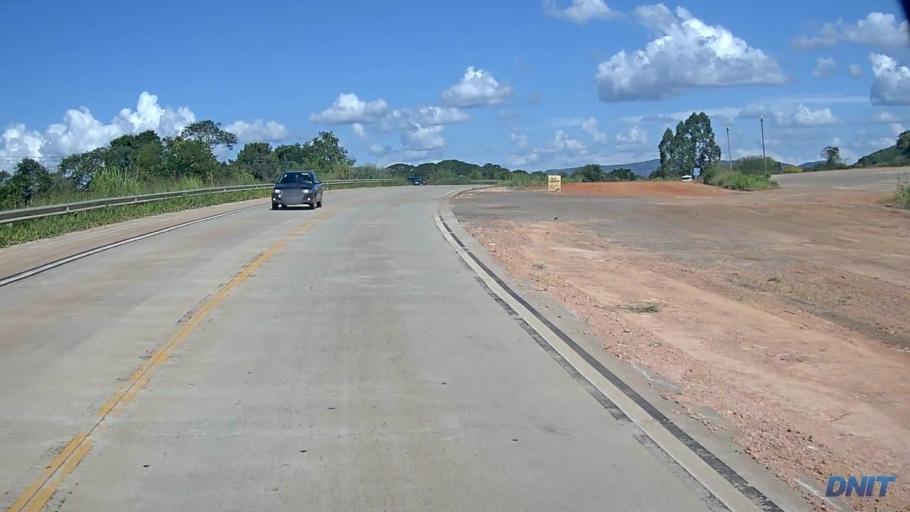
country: BR
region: Minas Gerais
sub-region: Barao De Cocais
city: Barao de Cocais
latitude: -19.7603
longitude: -43.4615
